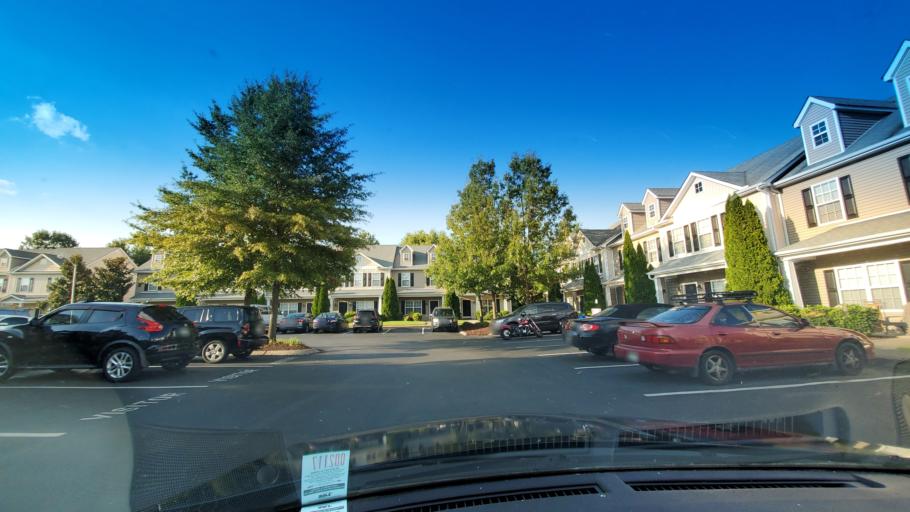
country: US
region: Tennessee
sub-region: Rutherford County
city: Murfreesboro
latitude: 35.7820
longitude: -86.4049
